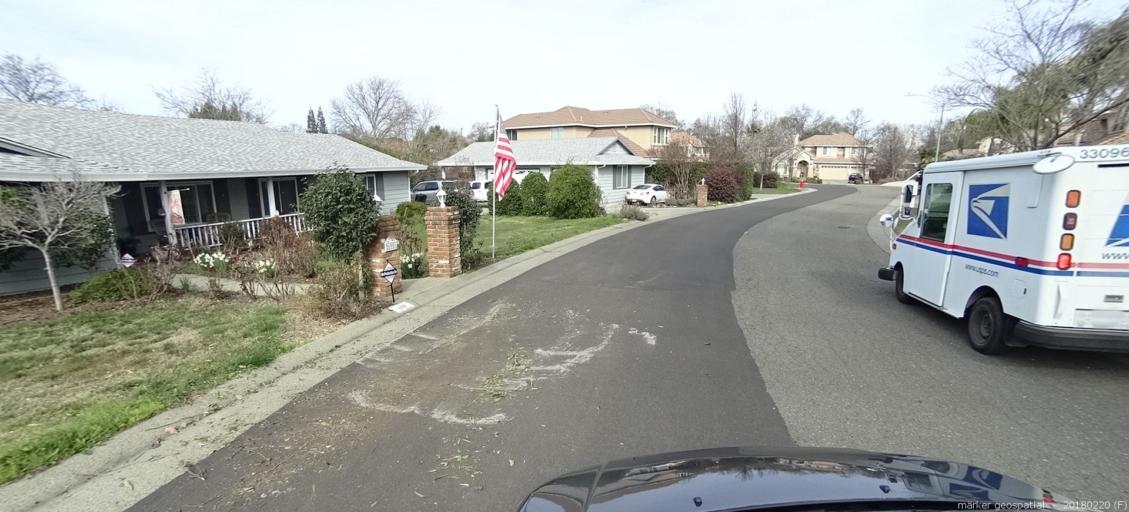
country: US
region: California
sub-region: Sacramento County
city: Orangevale
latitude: 38.6910
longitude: -121.2331
